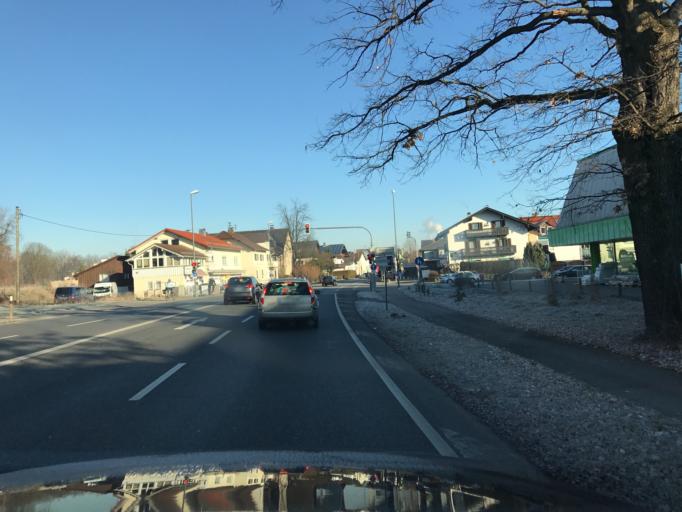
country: DE
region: Bavaria
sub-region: Upper Bavaria
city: Rosenheim
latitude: 47.8409
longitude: 12.1222
